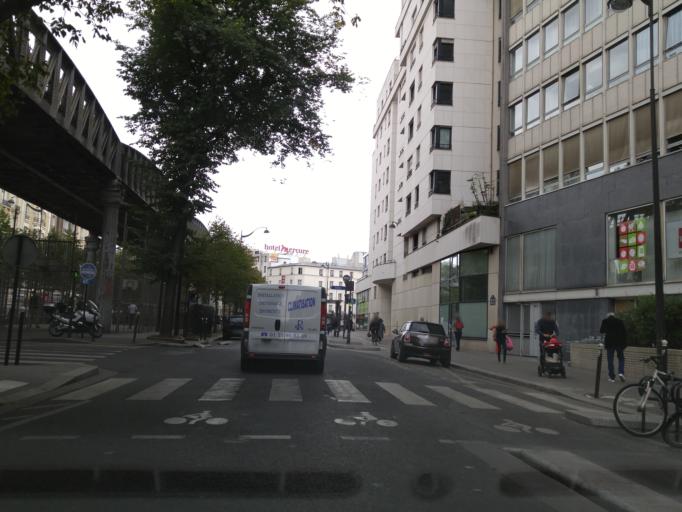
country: FR
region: Ile-de-France
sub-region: Departement des Hauts-de-Seine
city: Vanves
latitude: 48.8519
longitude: 2.2913
